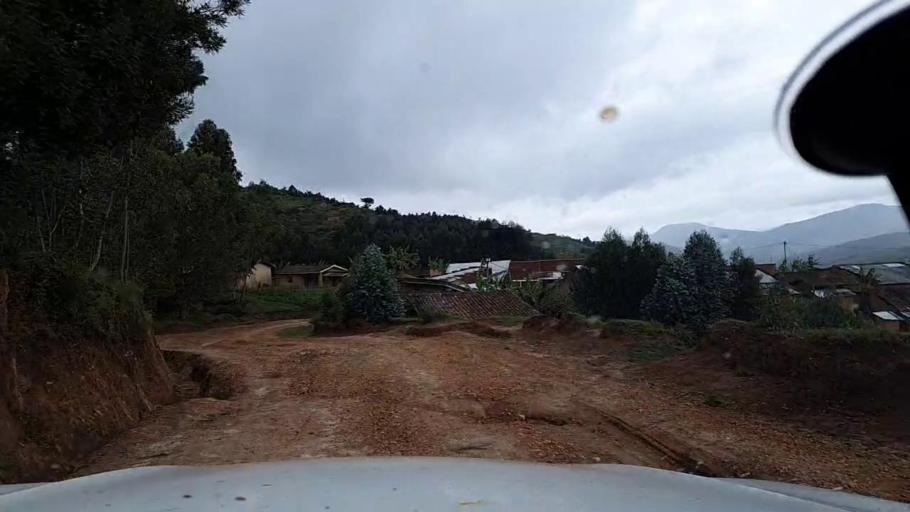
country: RW
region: Western Province
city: Kibuye
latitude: -2.0987
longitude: 29.4861
